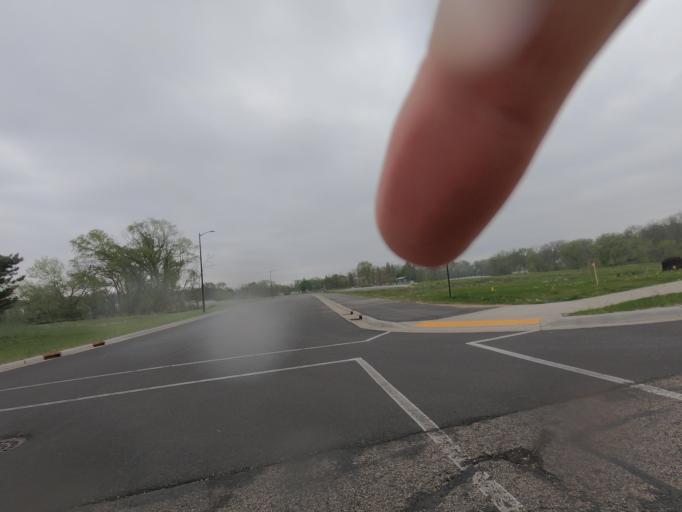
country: US
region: Wisconsin
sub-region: Jefferson County
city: Jefferson
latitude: 43.0130
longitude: -88.8108
